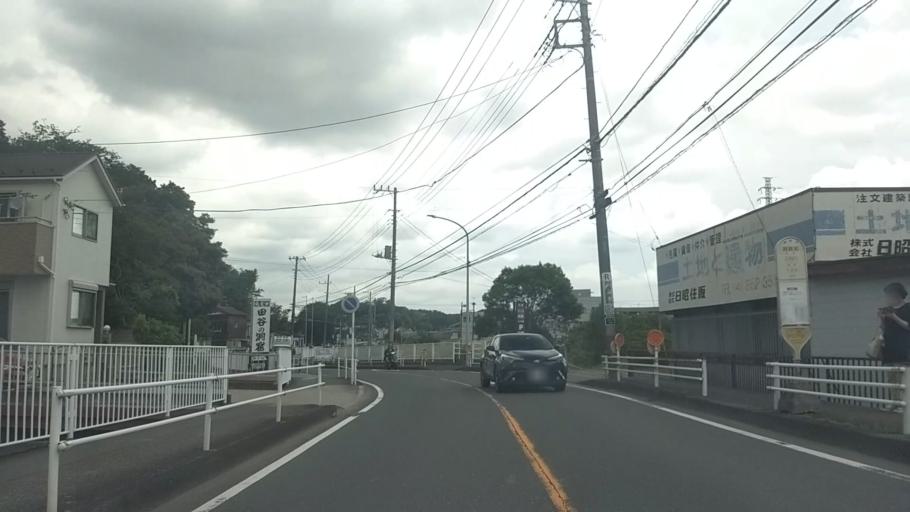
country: JP
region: Kanagawa
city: Fujisawa
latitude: 35.3673
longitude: 139.5226
